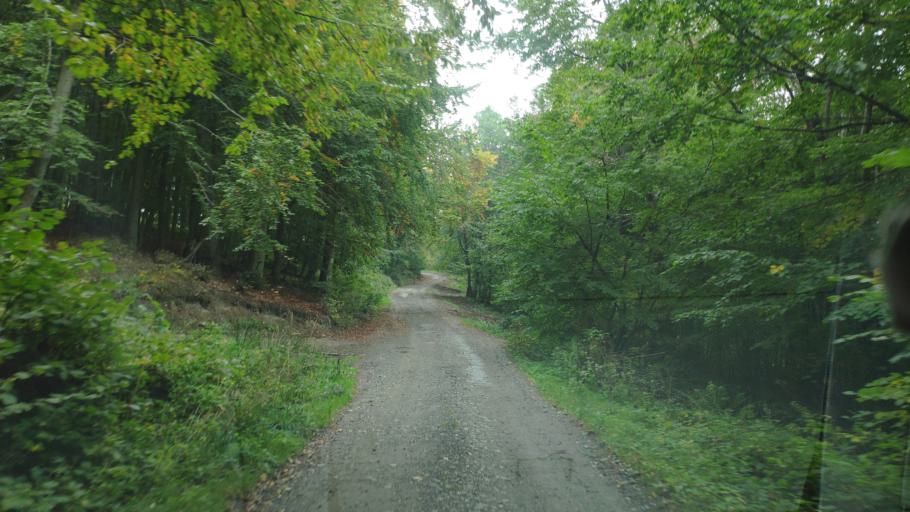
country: SK
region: Presovsky
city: Giraltovce
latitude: 48.9094
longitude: 21.4627
